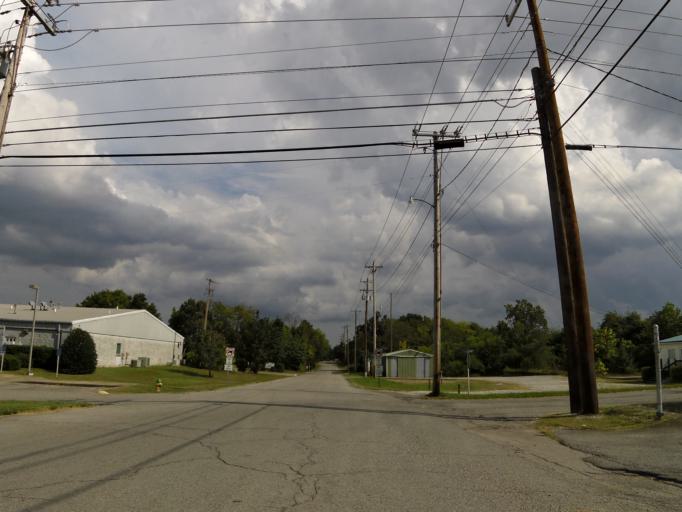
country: US
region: Tennessee
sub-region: Dickson County
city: Dickson
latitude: 36.0846
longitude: -87.3985
